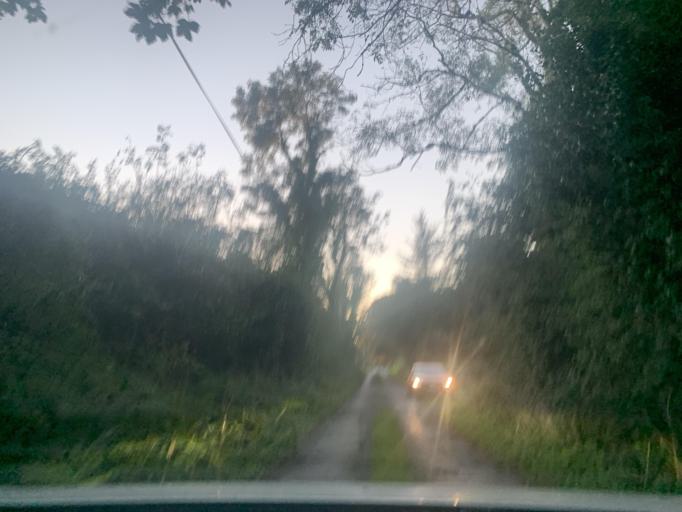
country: IE
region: Connaught
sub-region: Sligo
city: Sligo
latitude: 54.2749
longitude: -8.4193
